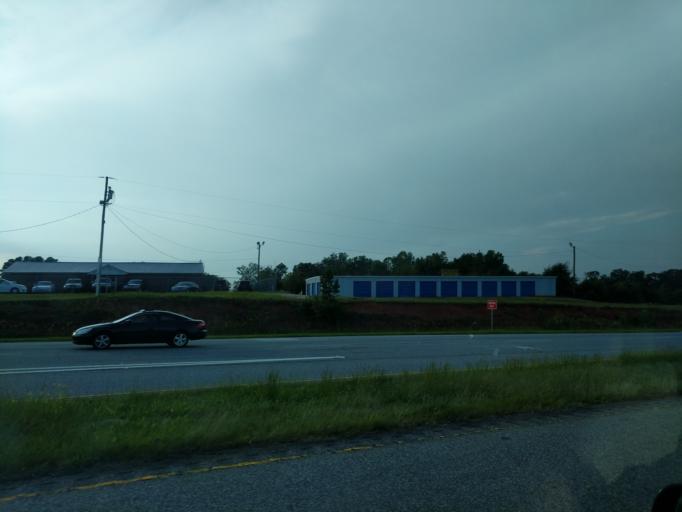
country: US
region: South Carolina
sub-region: Anderson County
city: Piedmont
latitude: 34.6772
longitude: -82.5089
